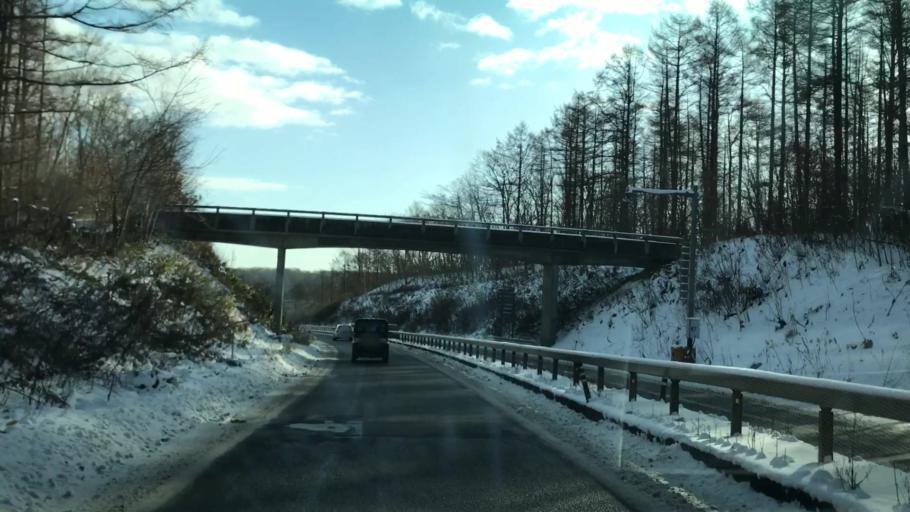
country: JP
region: Hokkaido
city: Chitose
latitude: 42.8107
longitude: 141.6278
